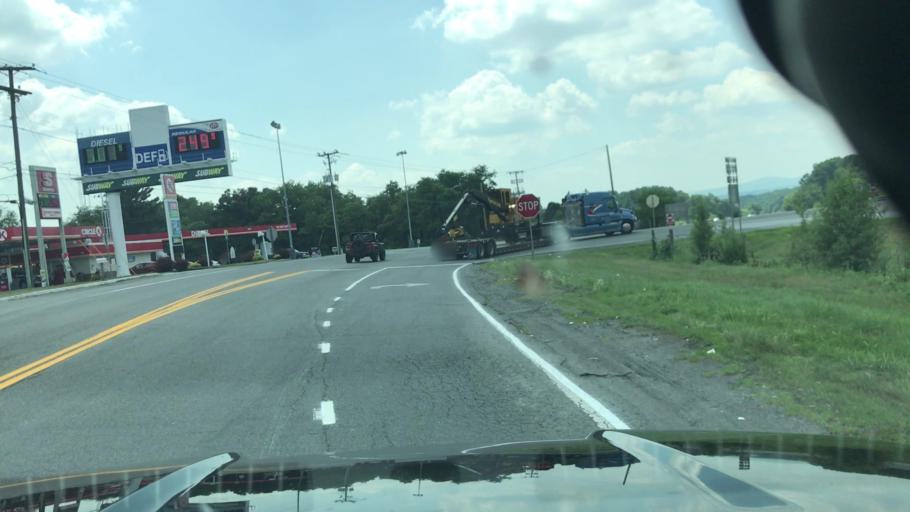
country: US
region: Virginia
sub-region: Wythe County
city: Wytheville
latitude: 36.9365
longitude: -80.9937
